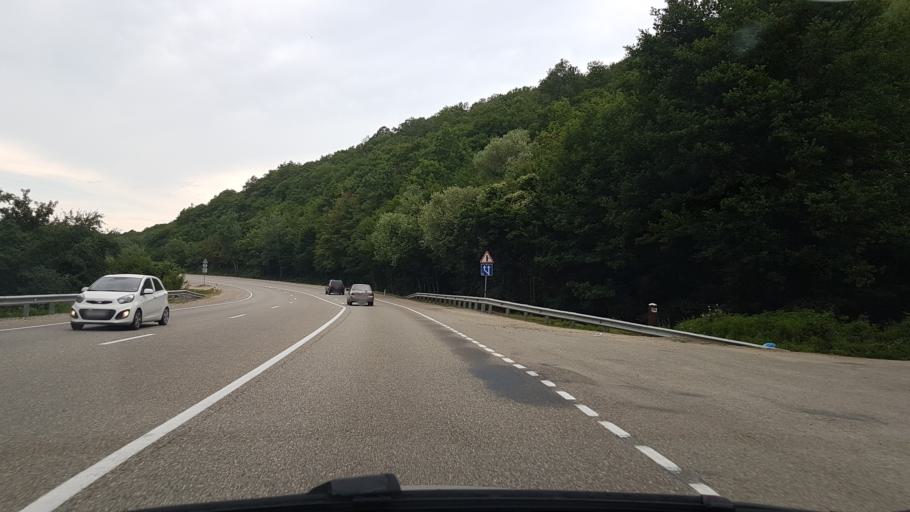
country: RU
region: Krasnodarskiy
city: Goryachiy Klyuch
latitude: 44.5212
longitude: 38.9197
